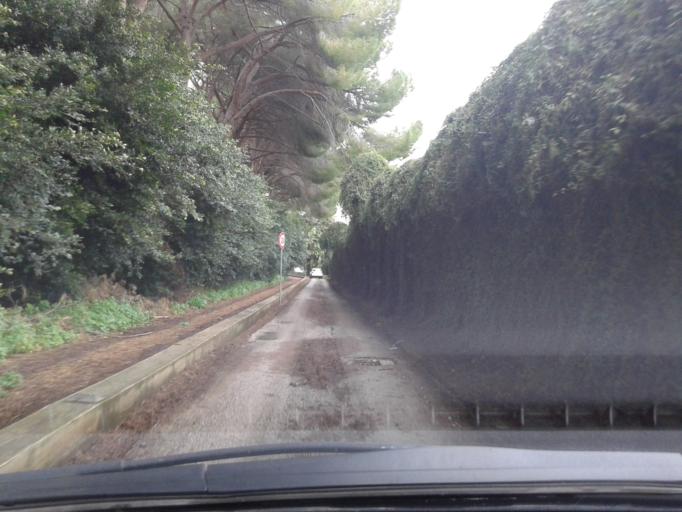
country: IT
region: Sicily
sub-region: Palermo
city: Monreale
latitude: 38.0936
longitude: 13.3116
